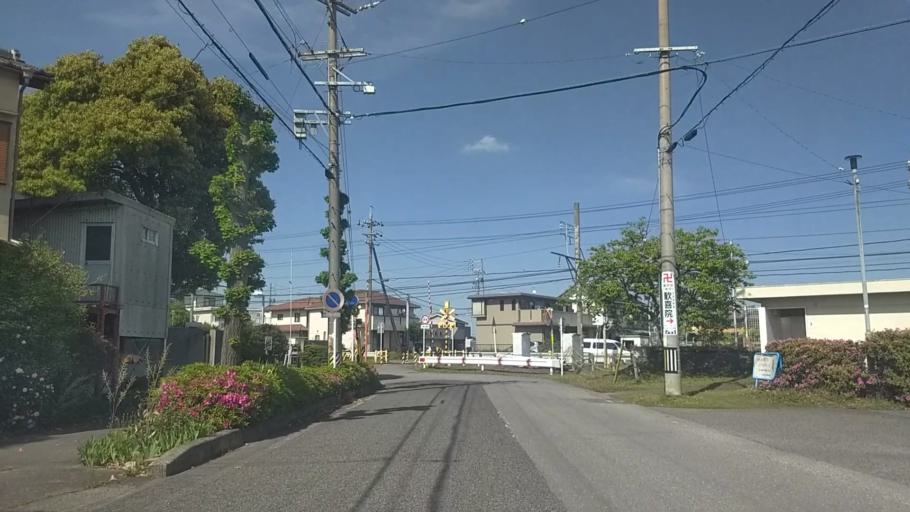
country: JP
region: Aichi
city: Anjo
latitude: 34.9649
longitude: 137.0917
